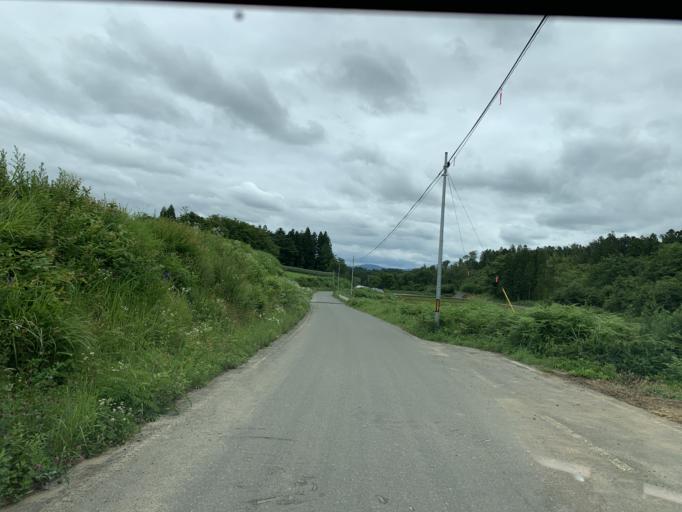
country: JP
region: Iwate
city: Ichinoseki
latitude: 38.9070
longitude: 141.0176
